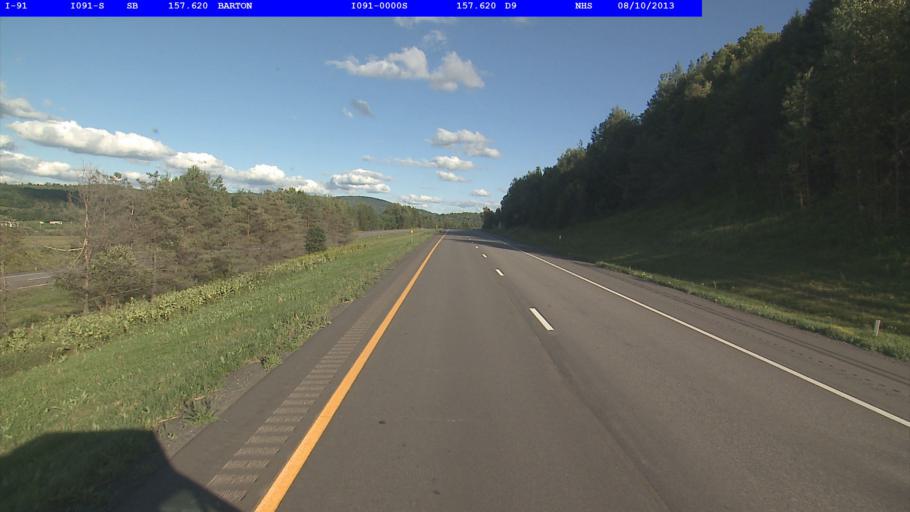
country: US
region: Vermont
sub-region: Orleans County
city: Newport
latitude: 44.7556
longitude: -72.1992
